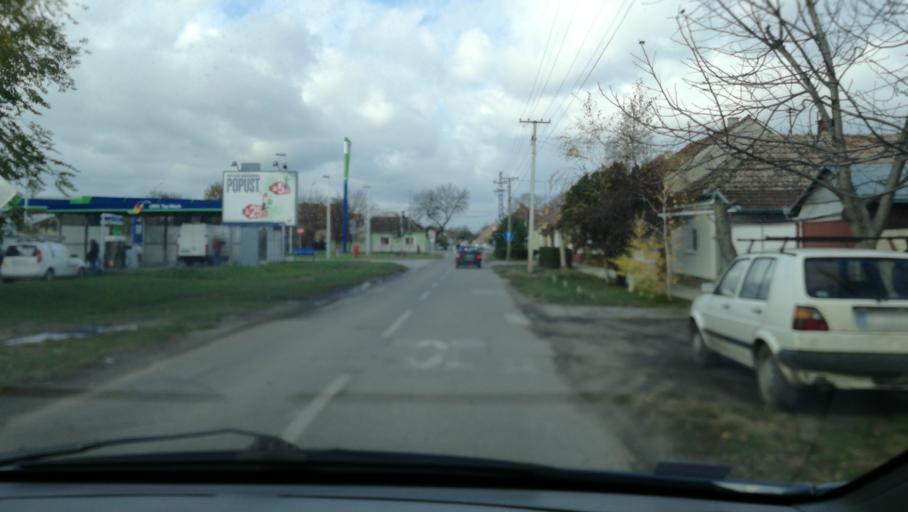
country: RS
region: Autonomna Pokrajina Vojvodina
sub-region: Severnobanatski Okrug
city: Kikinda
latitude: 45.8223
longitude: 20.4554
